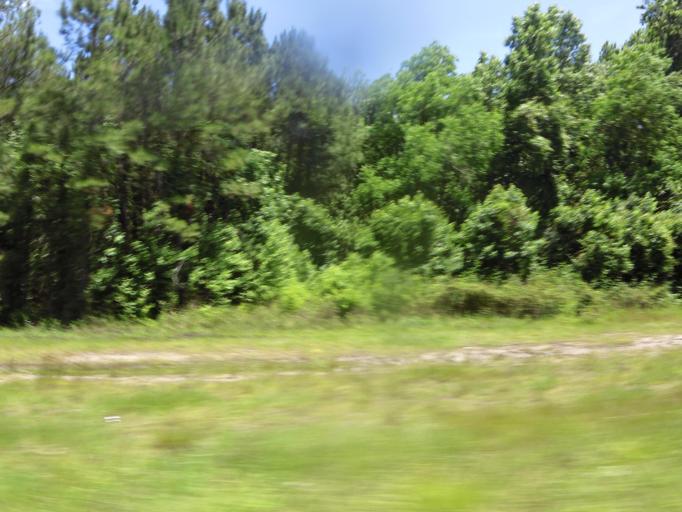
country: US
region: Florida
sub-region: Union County
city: Lake Butler
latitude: 30.0498
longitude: -82.2312
